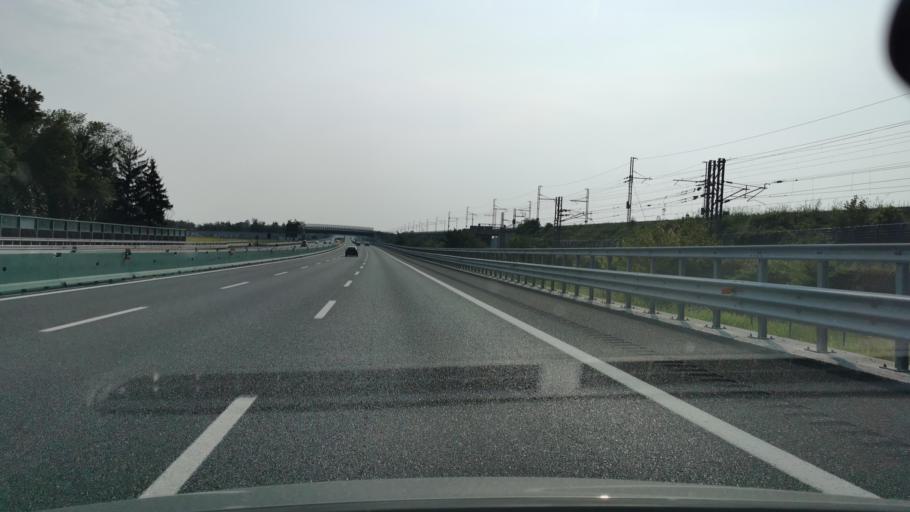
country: IT
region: Piedmont
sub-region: Provincia di Novara
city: Novara
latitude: 45.4683
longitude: 8.6308
